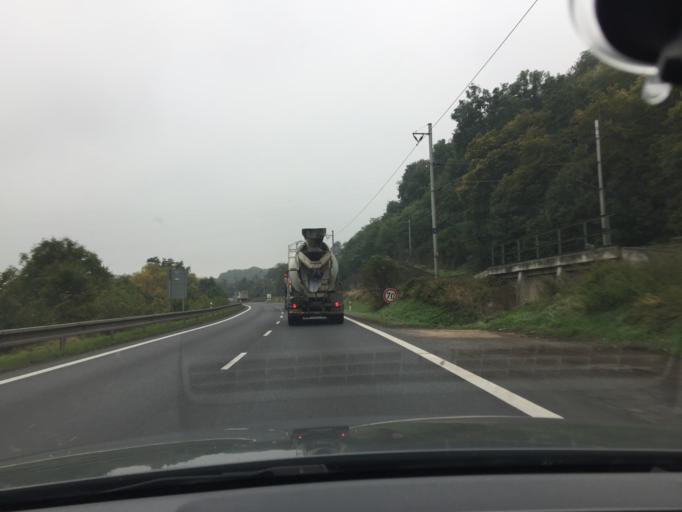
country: CZ
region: Ustecky
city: Trmice
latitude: 50.5874
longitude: 14.0298
